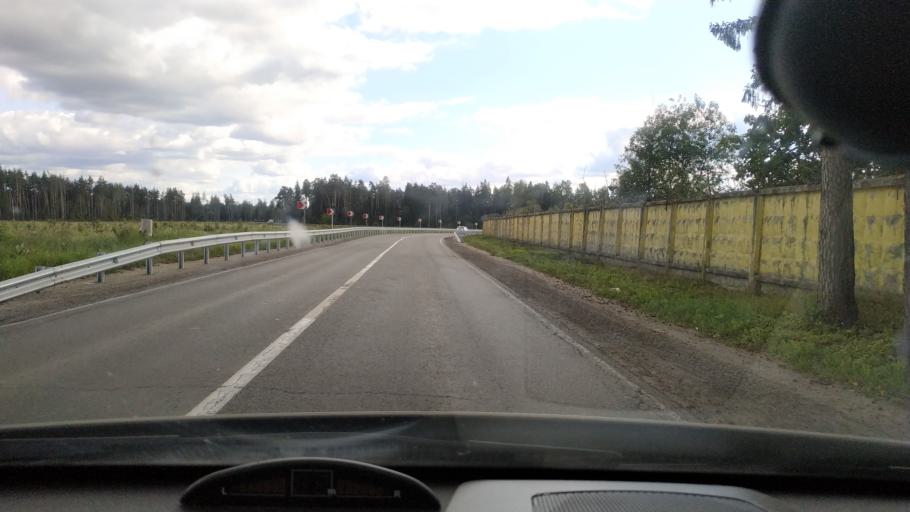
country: RU
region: Moskovskaya
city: Chornaya
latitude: 55.7724
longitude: 38.0530
